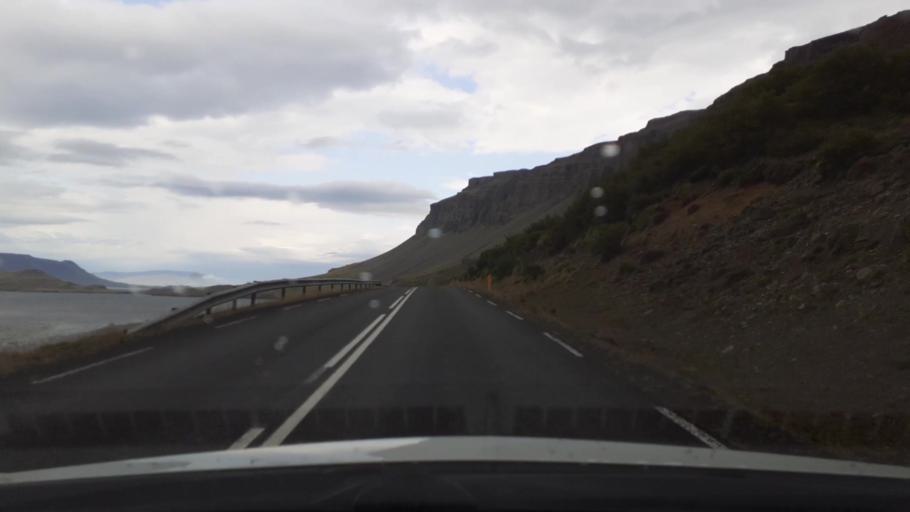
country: IS
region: Capital Region
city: Mosfellsbaer
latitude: 64.3881
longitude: -21.3631
